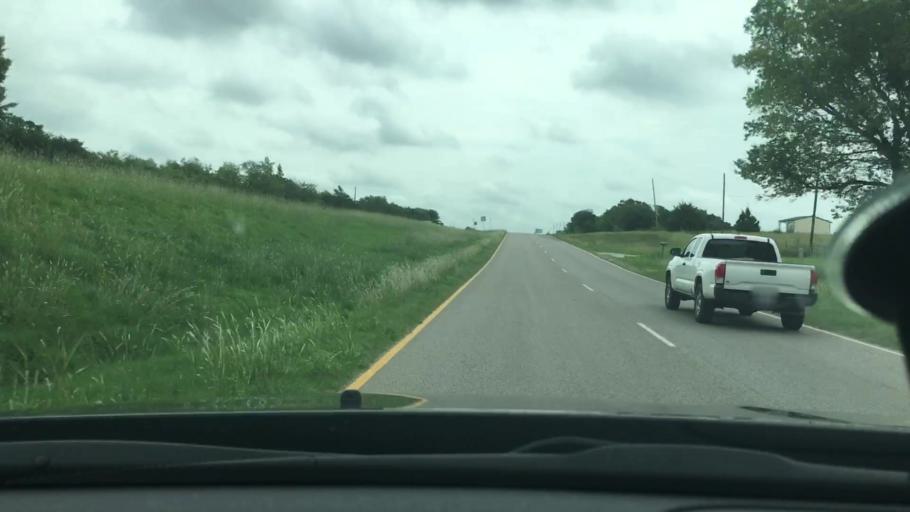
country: US
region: Oklahoma
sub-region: Carter County
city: Wilson
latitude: 34.1729
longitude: -97.4520
